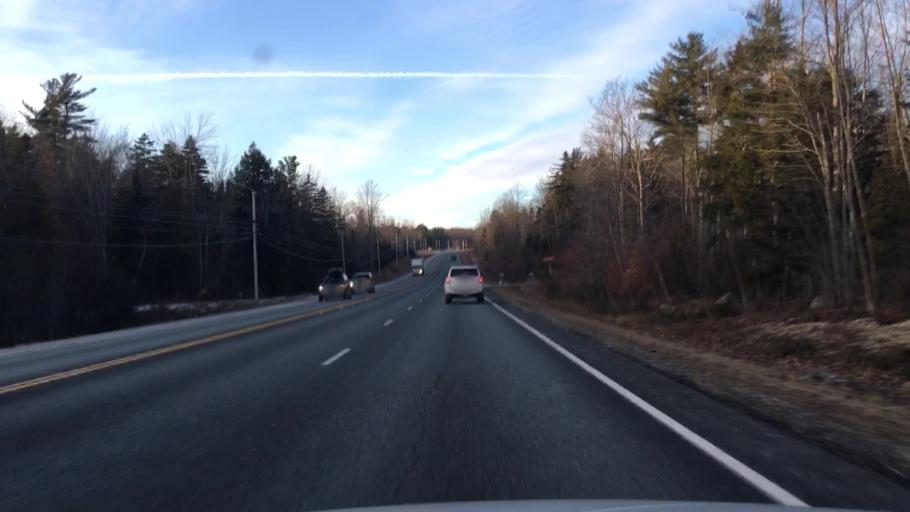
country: US
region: Maine
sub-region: Hancock County
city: Dedham
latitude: 44.6391
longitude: -68.5501
